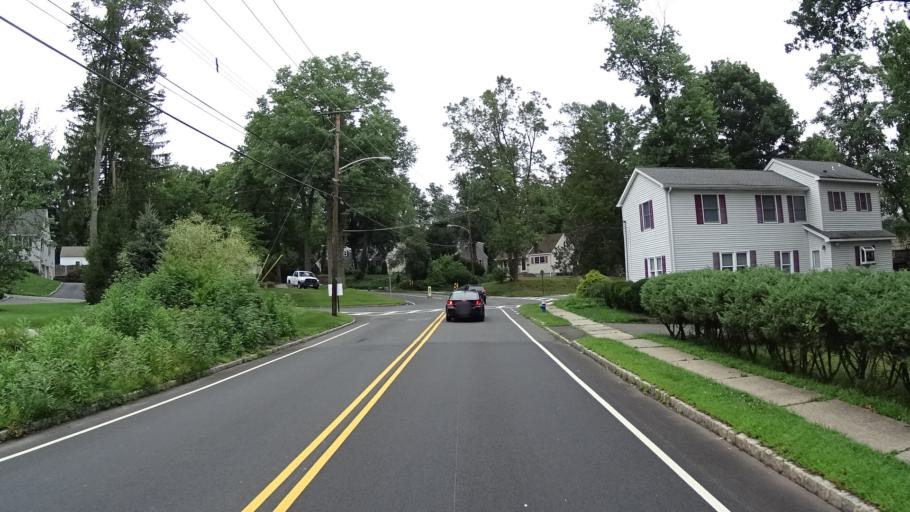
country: US
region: New Jersey
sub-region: Union County
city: New Providence
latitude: 40.6934
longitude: -74.4188
